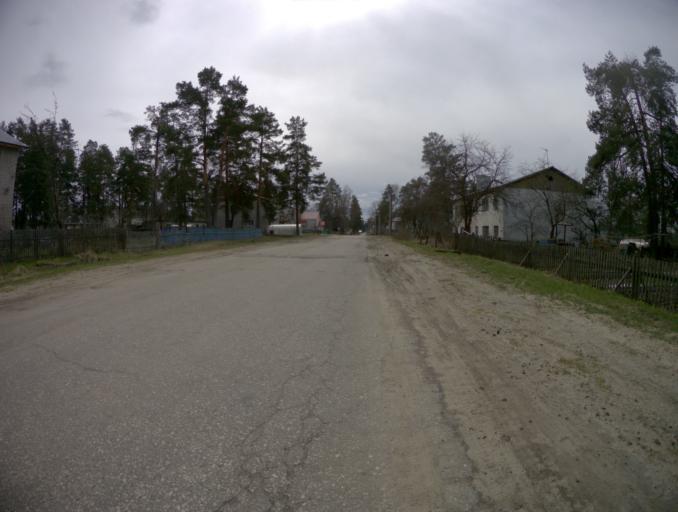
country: RU
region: Vladimir
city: Raduzhnyy
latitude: 55.9469
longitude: 40.2474
